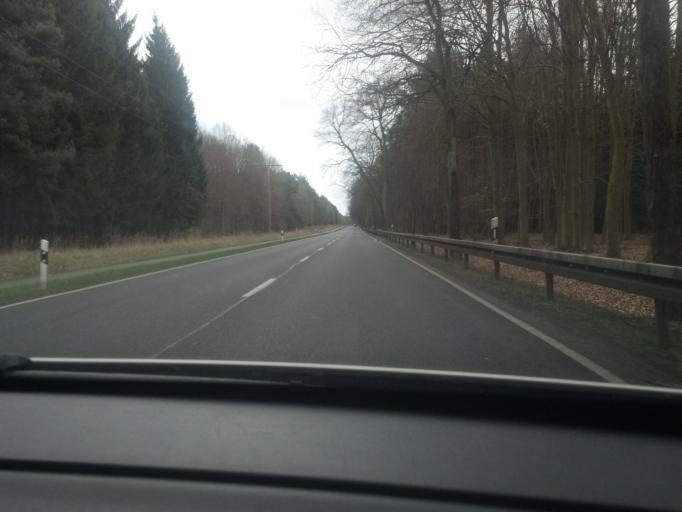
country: DE
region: Mecklenburg-Vorpommern
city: Wesenberg
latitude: 53.2716
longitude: 12.8586
